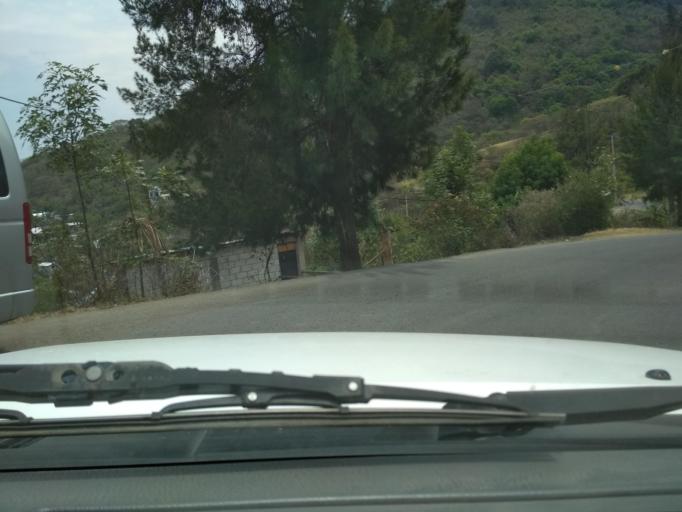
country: MX
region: Veracruz
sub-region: Camerino Z. Mendoza
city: La Cuesta
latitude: 18.7950
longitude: -97.1715
